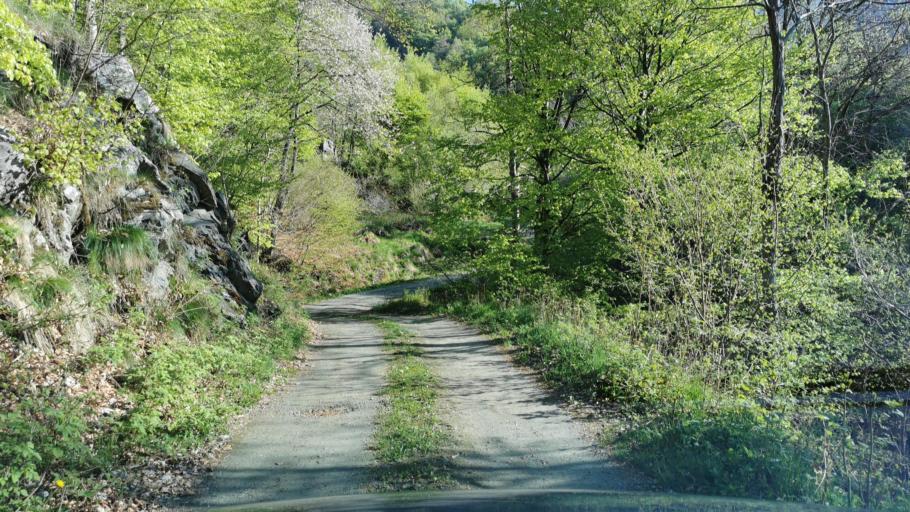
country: IT
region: Piedmont
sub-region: Provincia di Torino
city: Lemie
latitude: 45.2420
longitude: 7.2797
